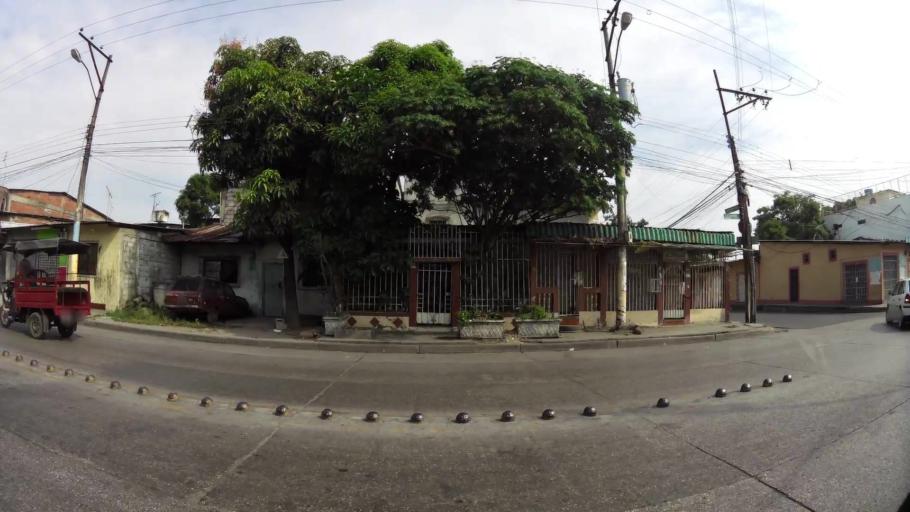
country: EC
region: Guayas
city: Guayaquil
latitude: -2.2546
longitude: -79.9046
